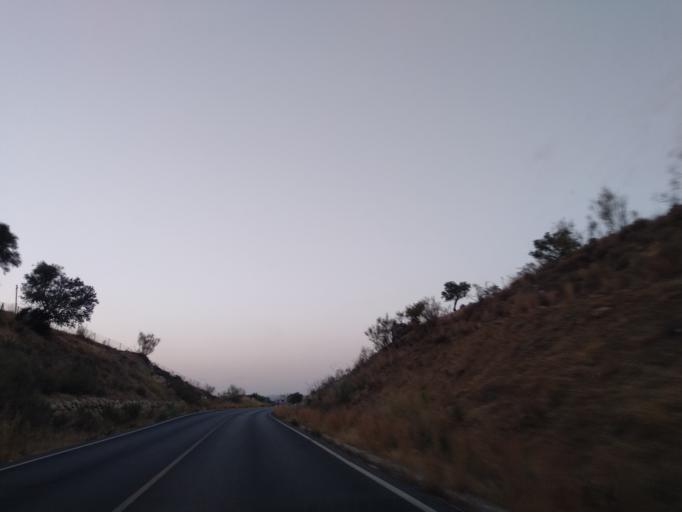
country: ES
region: Andalusia
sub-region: Provincia de Malaga
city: Cartama
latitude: 36.6945
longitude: -4.6511
